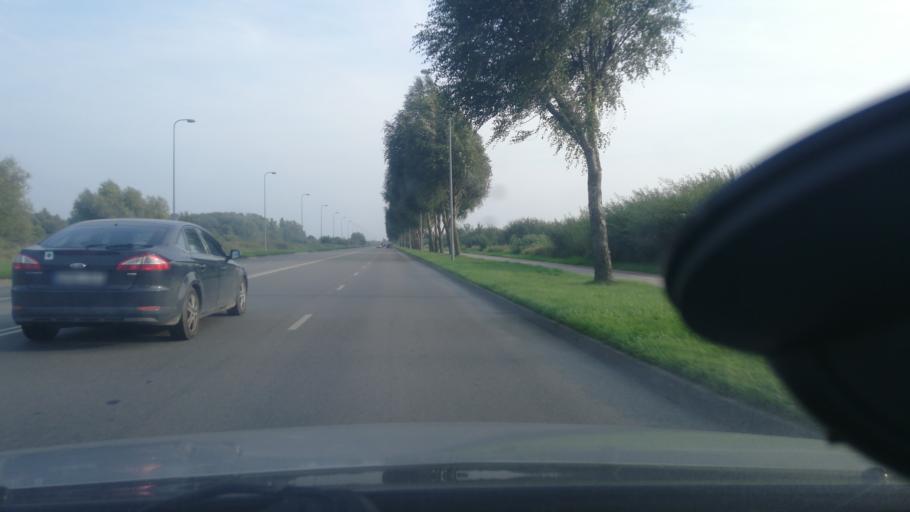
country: LT
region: Klaipedos apskritis
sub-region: Klaipeda
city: Klaipeda
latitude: 55.6614
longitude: 21.1666
